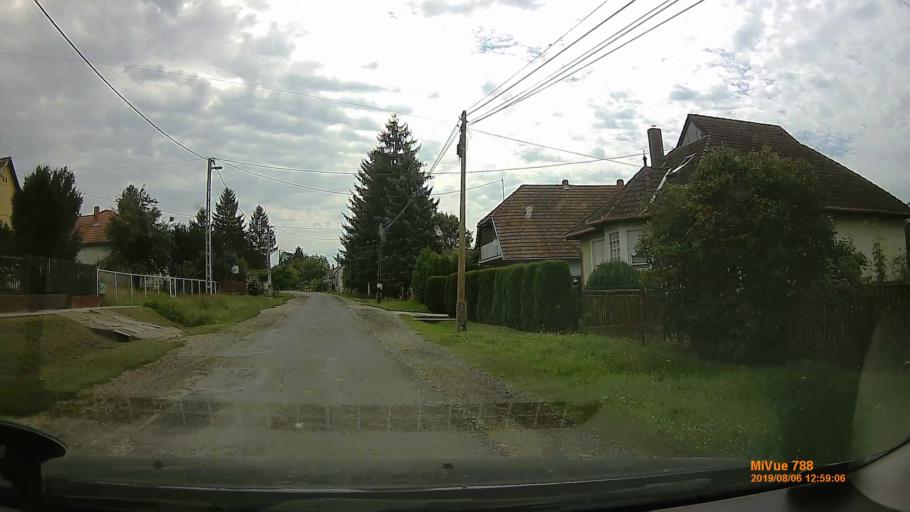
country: HU
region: Zala
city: Pacsa
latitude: 46.6258
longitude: 17.0454
